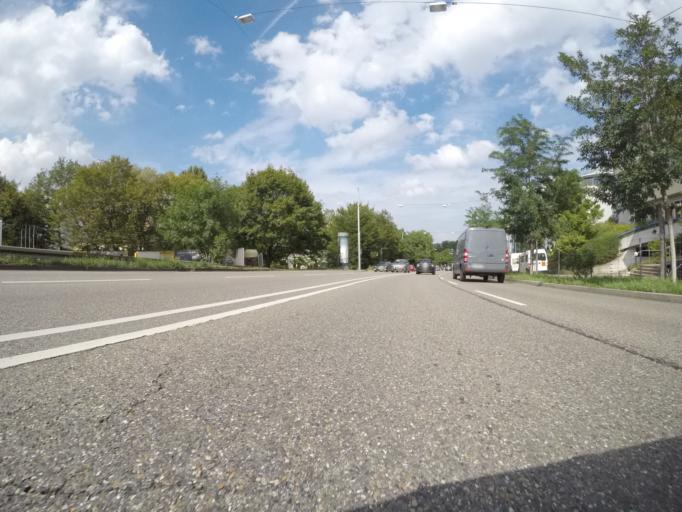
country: DE
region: Baden-Wuerttemberg
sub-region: Regierungsbezirk Stuttgart
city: Stuttgart
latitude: 48.7535
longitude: 9.1724
